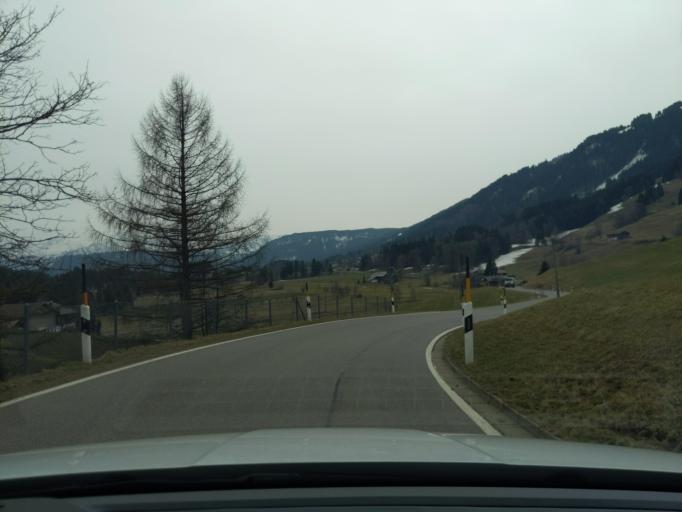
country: DE
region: Bavaria
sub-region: Swabia
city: Ofterschwang
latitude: 47.4876
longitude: 10.2343
